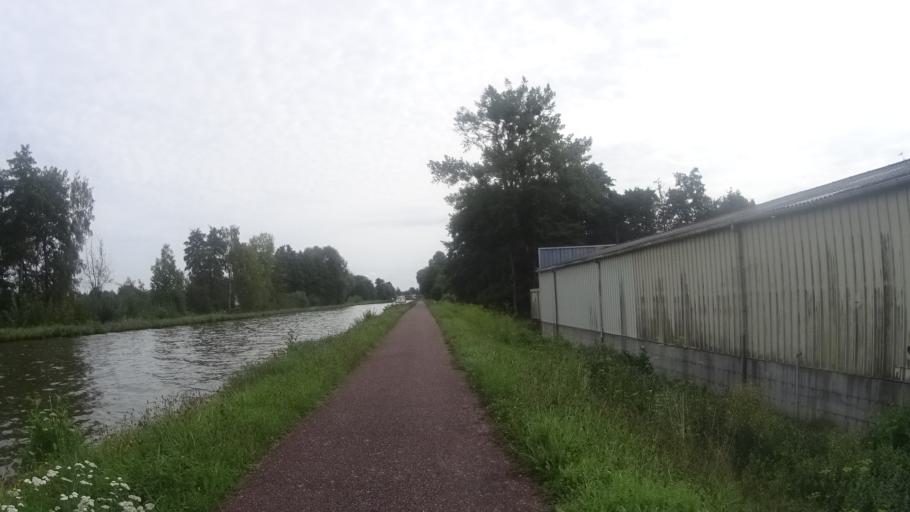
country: FR
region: Alsace
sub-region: Departement du Bas-Rhin
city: Steinbourg
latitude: 48.7607
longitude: 7.4099
